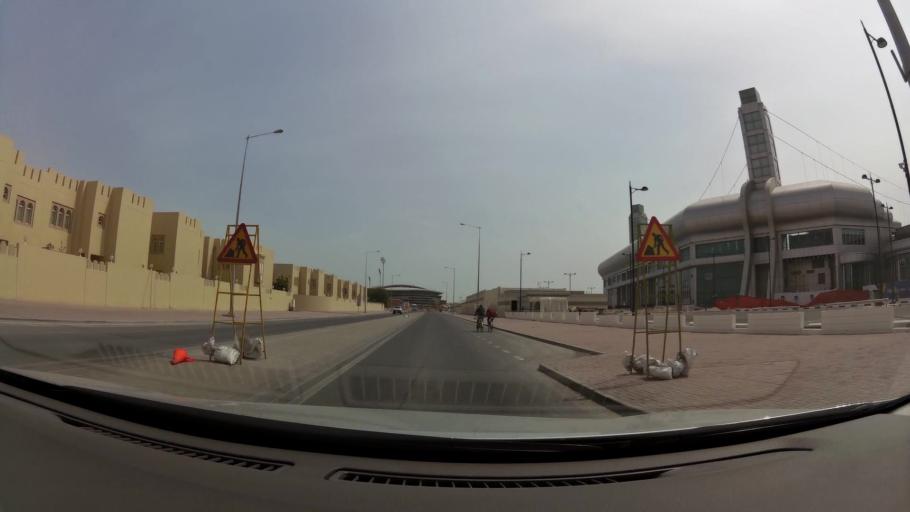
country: QA
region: Baladiyat ad Dawhah
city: Doha
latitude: 25.2685
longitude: 51.4831
